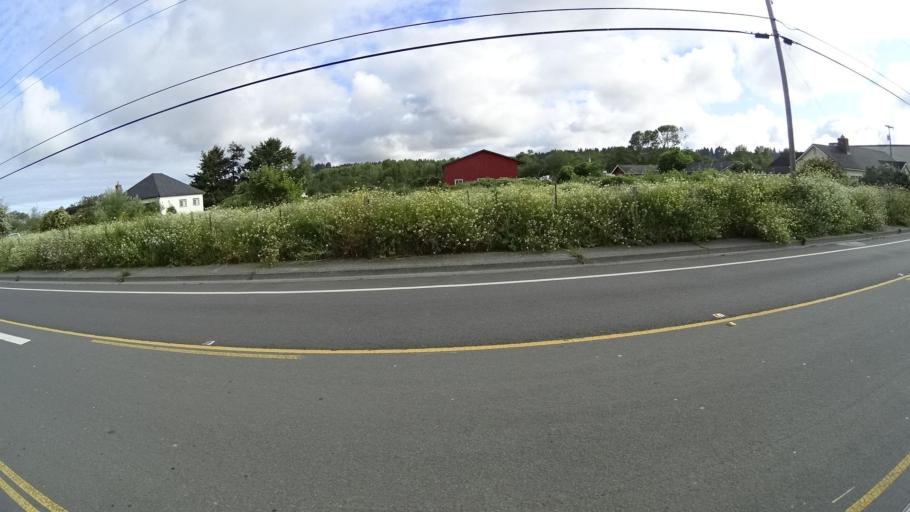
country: US
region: California
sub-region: Humboldt County
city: Arcata
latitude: 40.9050
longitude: -124.0819
